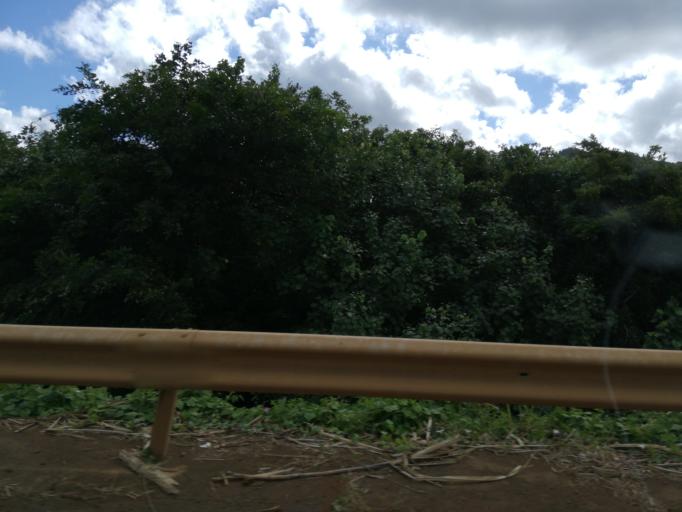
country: MU
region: Grand Port
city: Bois des Amourettes
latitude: -20.3691
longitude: 57.7020
